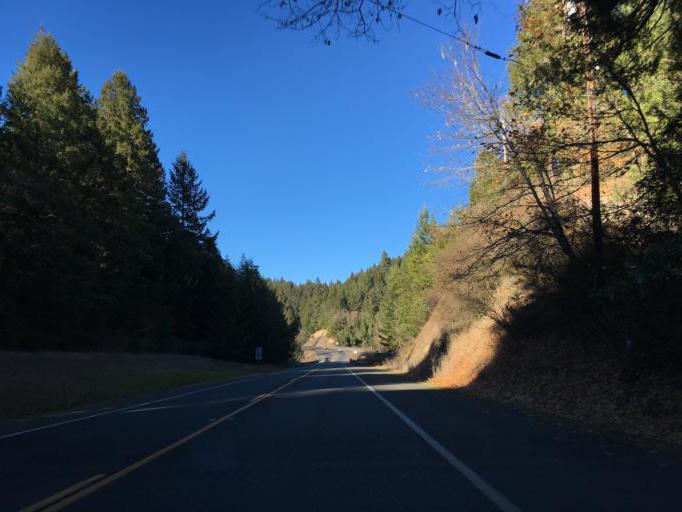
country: US
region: California
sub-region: Mendocino County
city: Brooktrails
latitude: 39.4612
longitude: -123.3499
